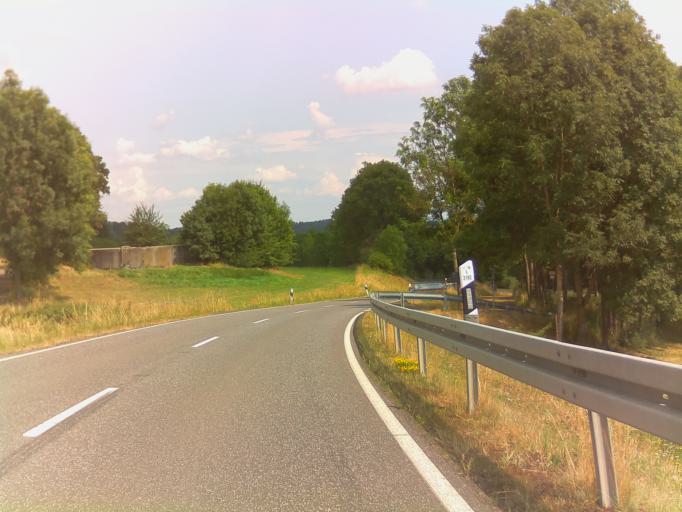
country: DE
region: Hesse
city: Herbstein
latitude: 50.5386
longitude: 9.3975
